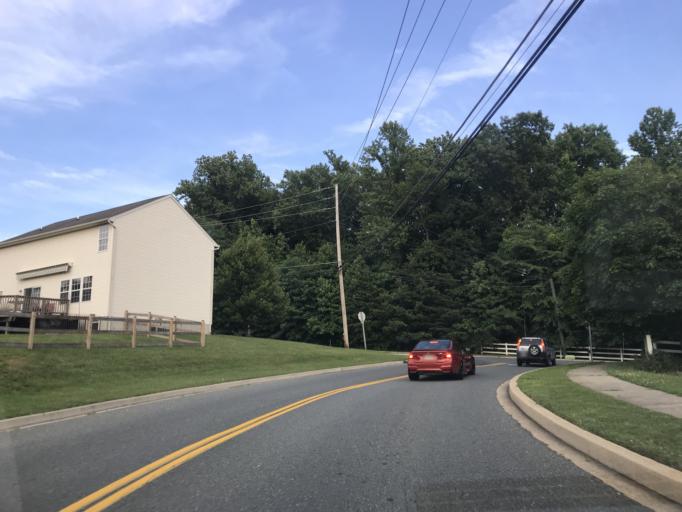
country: US
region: Maryland
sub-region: Harford County
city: Aberdeen
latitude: 39.5151
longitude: -76.1884
